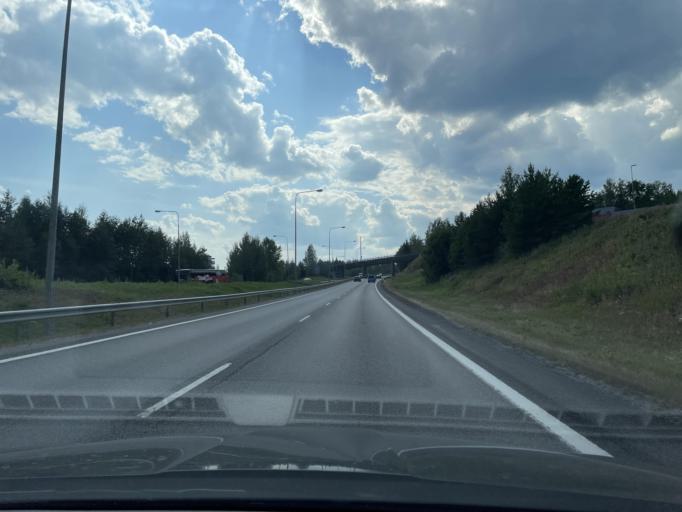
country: FI
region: Central Finland
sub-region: Jyvaeskylae
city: Jyvaeskylae
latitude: 62.2134
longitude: 25.7225
